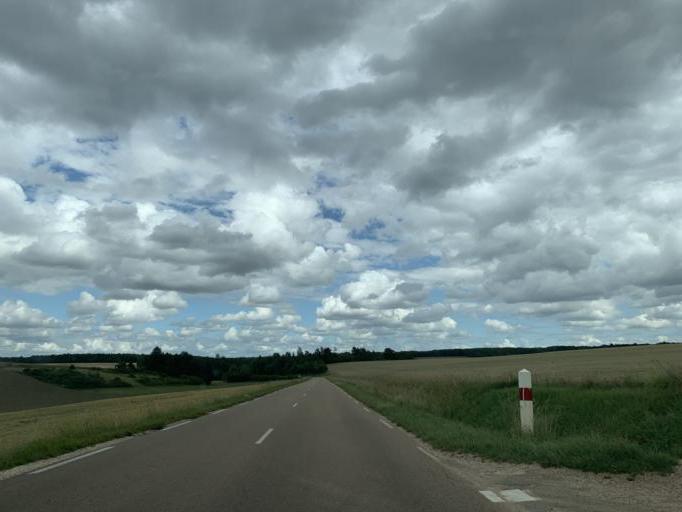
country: FR
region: Bourgogne
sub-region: Departement de l'Yonne
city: Chablis
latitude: 47.7349
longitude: 3.7885
